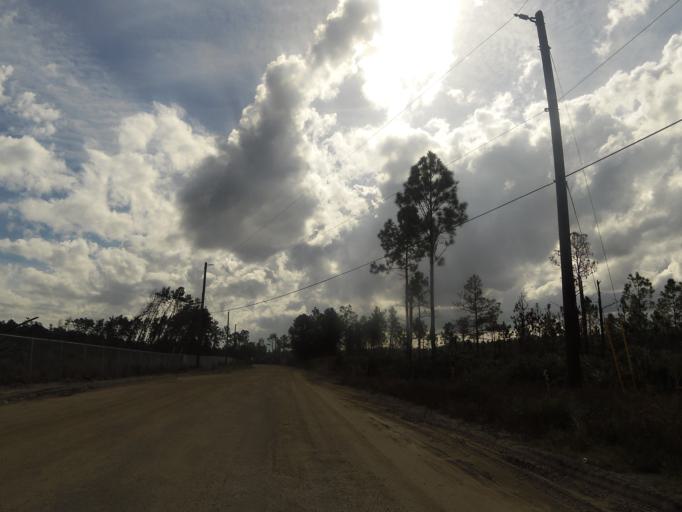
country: US
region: Florida
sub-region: Saint Johns County
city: Villano Beach
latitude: 29.9872
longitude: -81.3879
